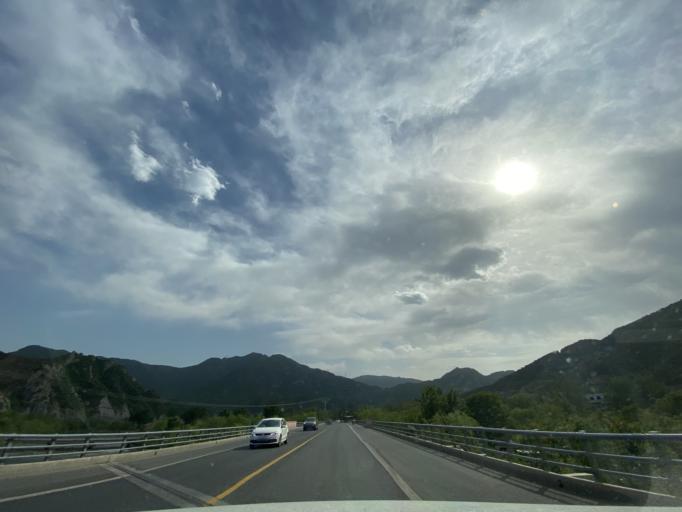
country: CN
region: Beijing
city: Miaofengshan
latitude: 39.9806
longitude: 116.0601
